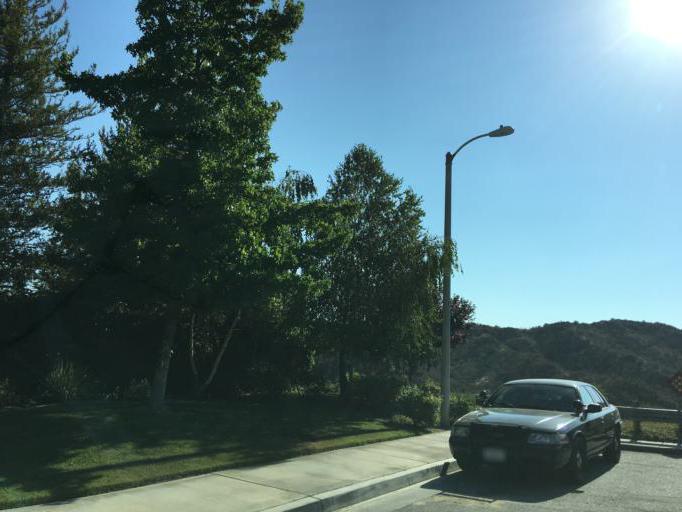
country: US
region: California
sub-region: Los Angeles County
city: Santa Clarita
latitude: 34.3773
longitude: -118.5814
